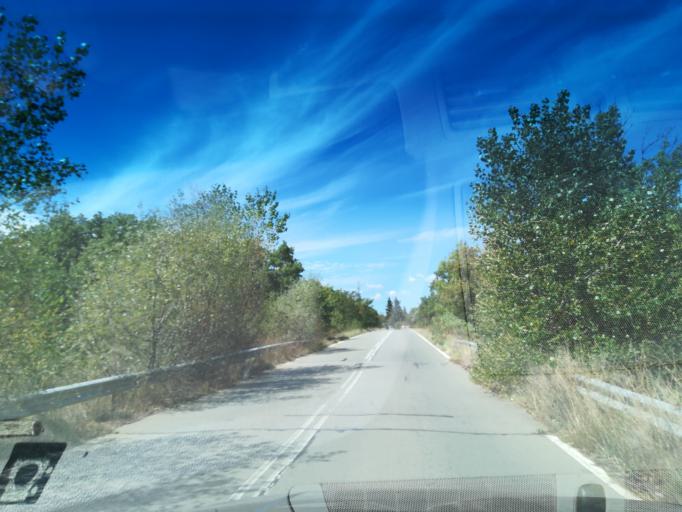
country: BG
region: Plovdiv
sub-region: Obshtina Suedinenie
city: Suedinenie
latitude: 42.3923
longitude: 24.5669
